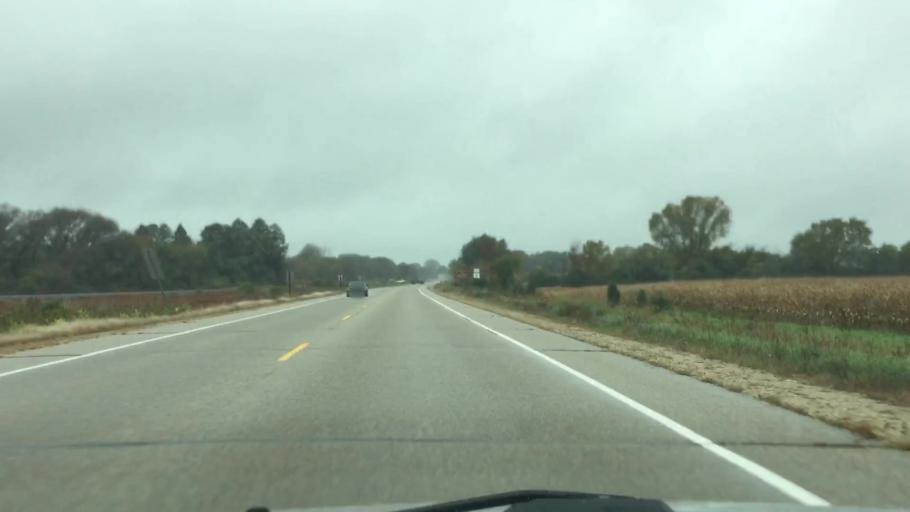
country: US
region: Wisconsin
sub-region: Jefferson County
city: Palmyra
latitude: 42.8792
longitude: -88.5384
